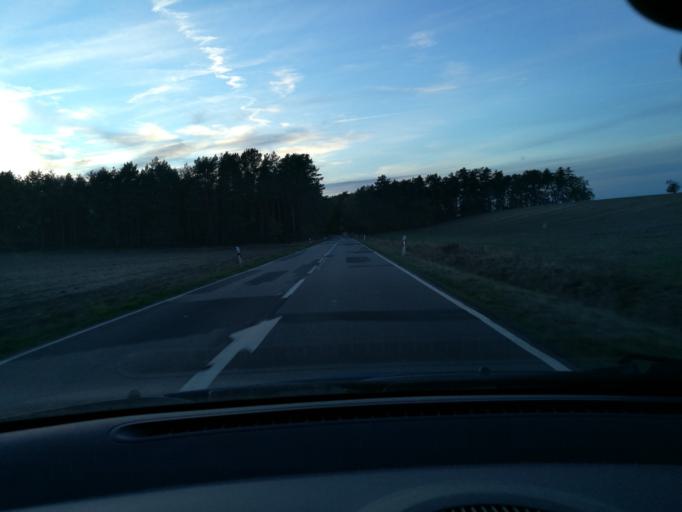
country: DE
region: Brandenburg
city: Lenzen
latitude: 53.1005
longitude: 11.5235
